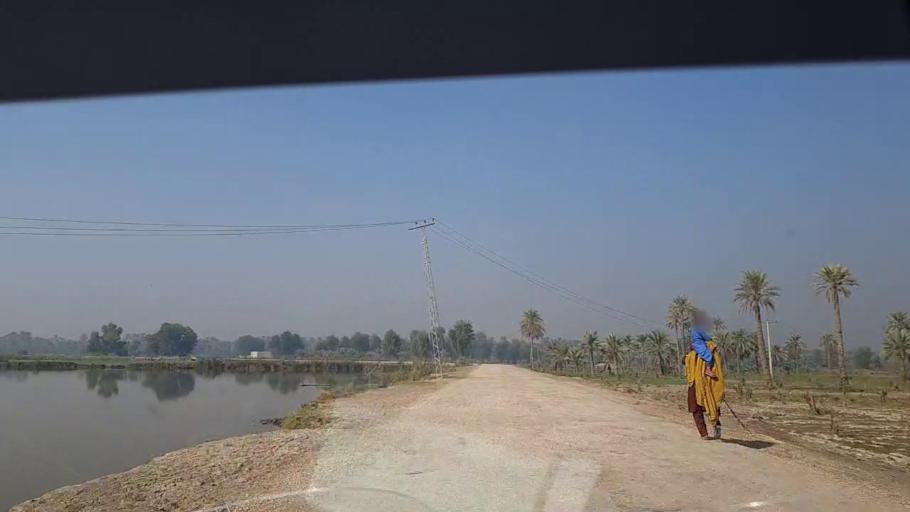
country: PK
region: Sindh
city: Khairpur
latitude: 27.4920
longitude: 68.7497
